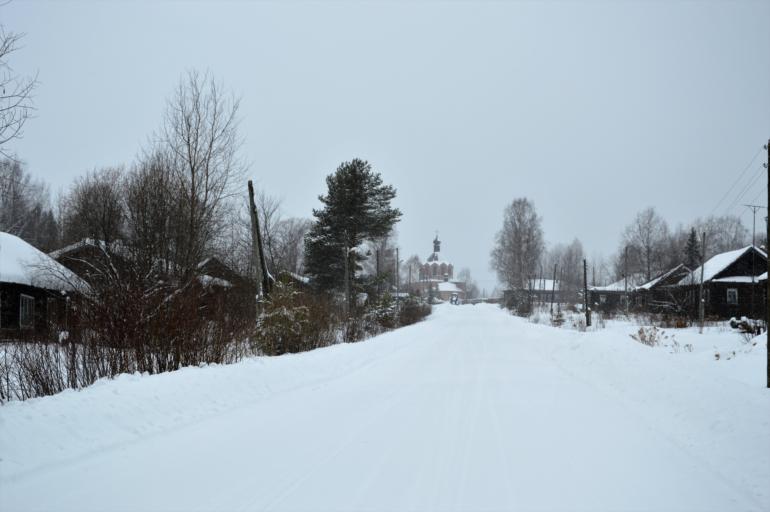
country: RU
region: Kostroma
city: Bogovarovo
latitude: 58.8328
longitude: 47.3981
